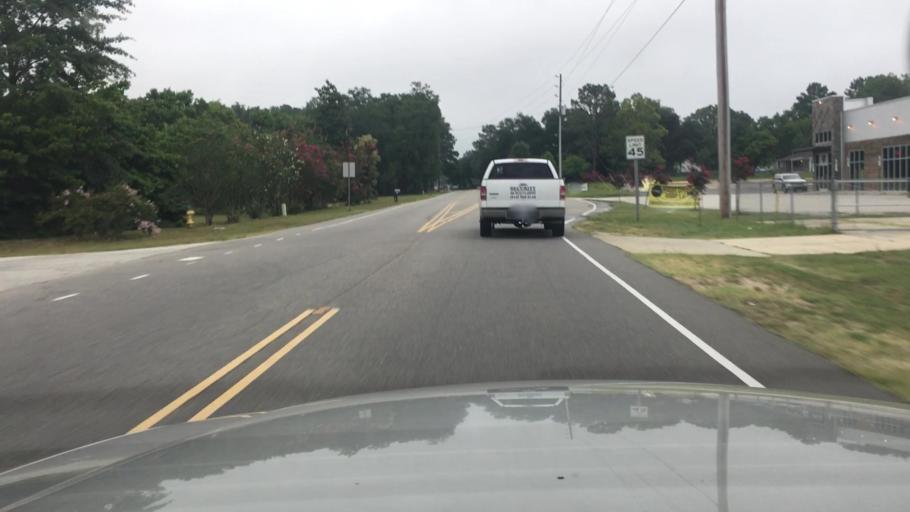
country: US
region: North Carolina
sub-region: Cumberland County
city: Hope Mills
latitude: 34.9754
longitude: -78.9974
